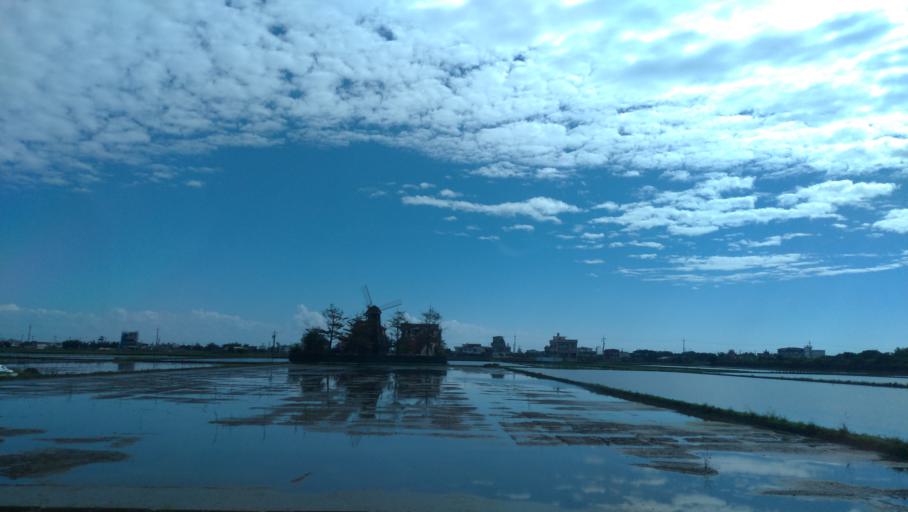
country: TW
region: Taiwan
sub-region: Yilan
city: Yilan
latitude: 24.8006
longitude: 121.7878
